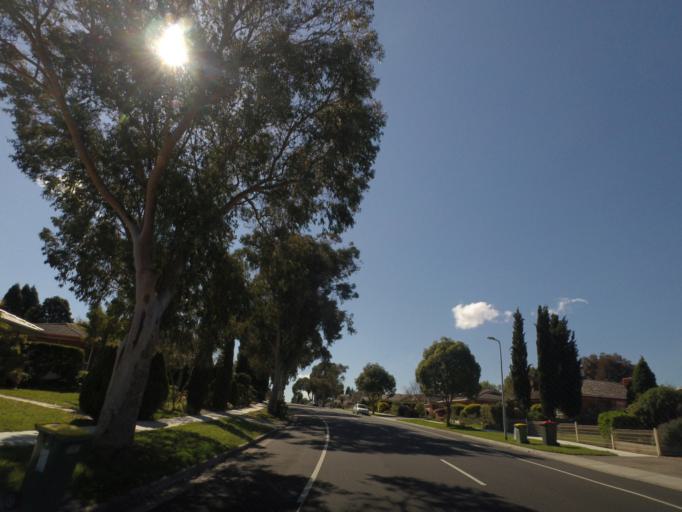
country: AU
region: Victoria
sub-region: Knox
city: Wantirna South
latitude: -37.8693
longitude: 145.2249
